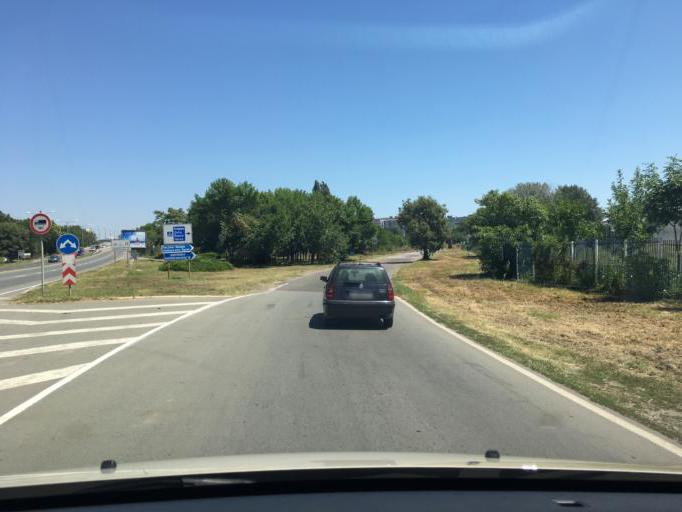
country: BG
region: Burgas
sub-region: Obshtina Burgas
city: Burgas
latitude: 42.4960
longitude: 27.4533
